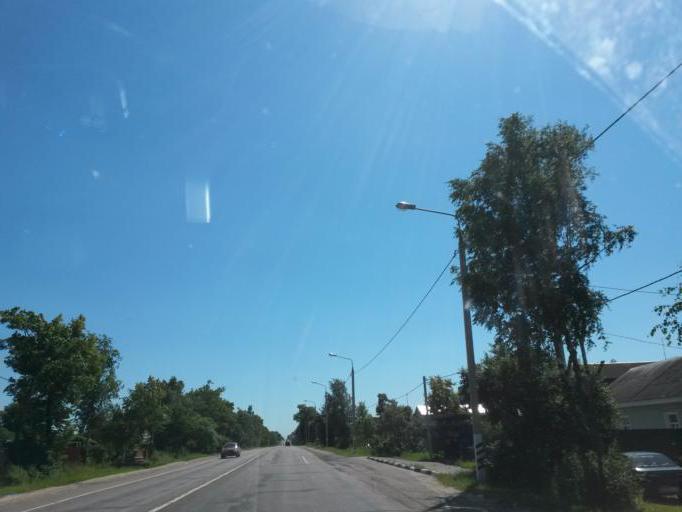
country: RU
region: Moskovskaya
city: Proletarskiy
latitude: 55.0745
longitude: 37.4383
